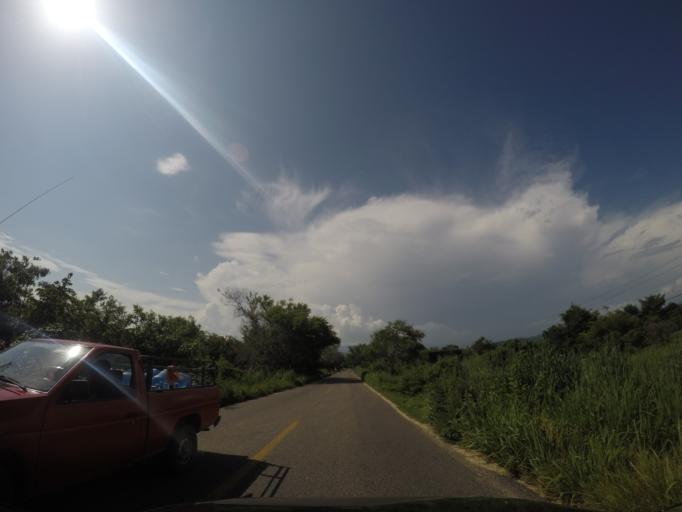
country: MX
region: Oaxaca
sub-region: San Pedro Mixtepec -Dto. 22 -
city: Puerto Escondido
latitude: 15.9063
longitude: -97.1179
